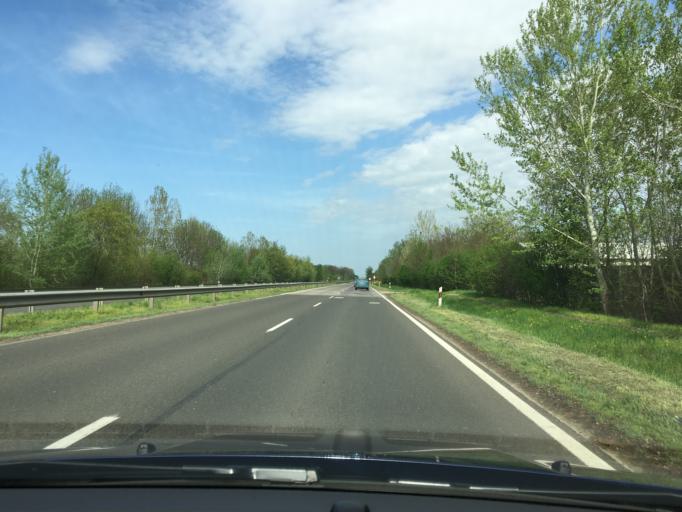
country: HU
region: Csongrad
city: Algyo
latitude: 46.3746
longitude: 20.2362
